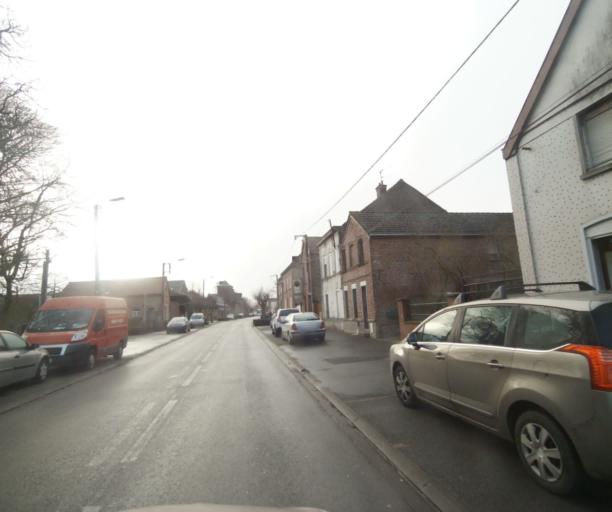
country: FR
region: Nord-Pas-de-Calais
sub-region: Departement du Nord
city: Famars
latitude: 50.3181
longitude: 3.5185
